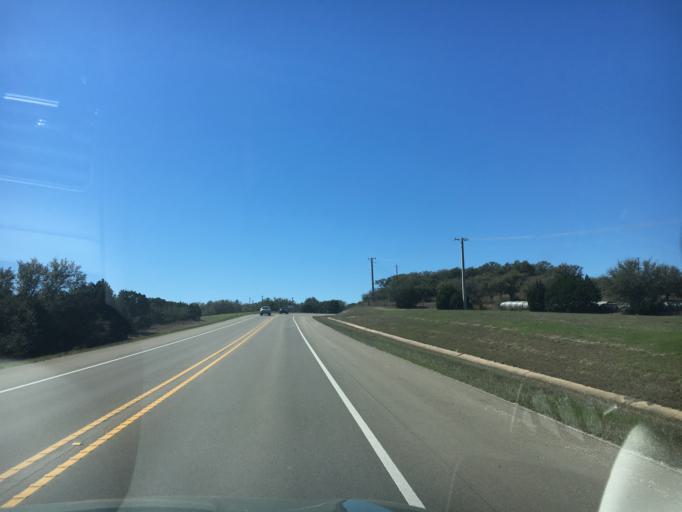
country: US
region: Texas
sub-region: Travis County
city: The Hills
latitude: 30.2863
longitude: -98.0601
